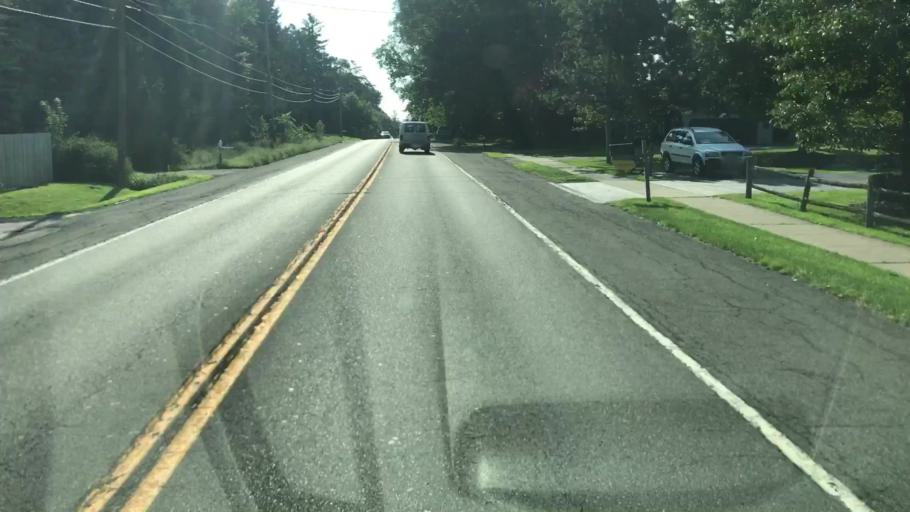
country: US
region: New York
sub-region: Onondaga County
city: Manlius
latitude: 43.0093
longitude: -75.9926
